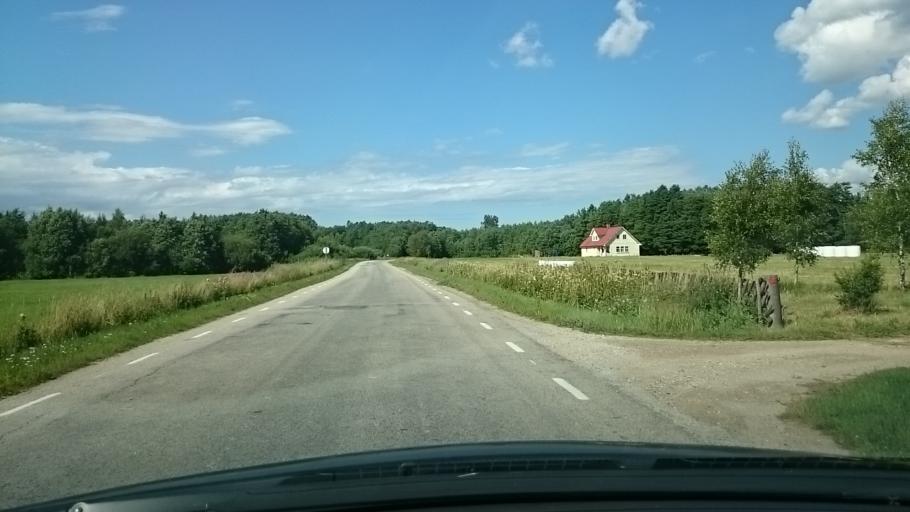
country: EE
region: Laeaene
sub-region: Haapsalu linn
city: Haapsalu
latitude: 59.0406
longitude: 23.5091
